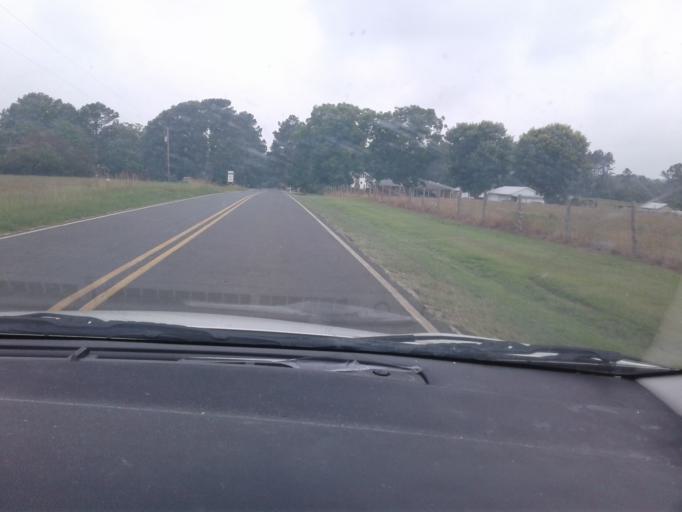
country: US
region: North Carolina
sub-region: Harnett County
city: Coats
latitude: 35.3763
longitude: -78.6483
